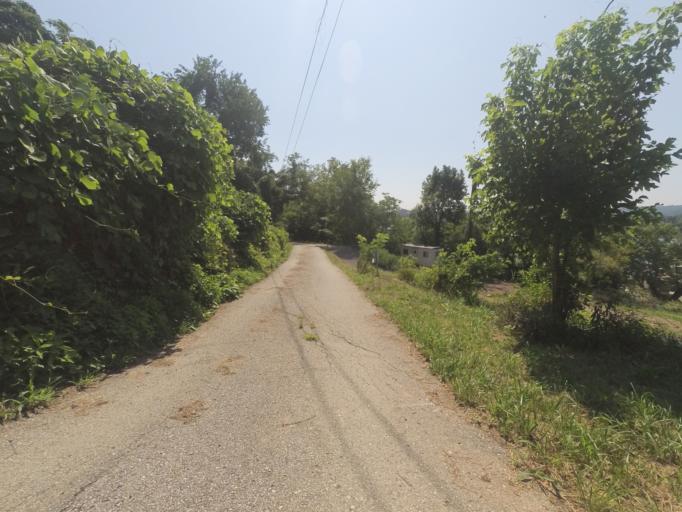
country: US
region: West Virginia
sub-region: Cabell County
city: Huntington
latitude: 38.4318
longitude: -82.4376
